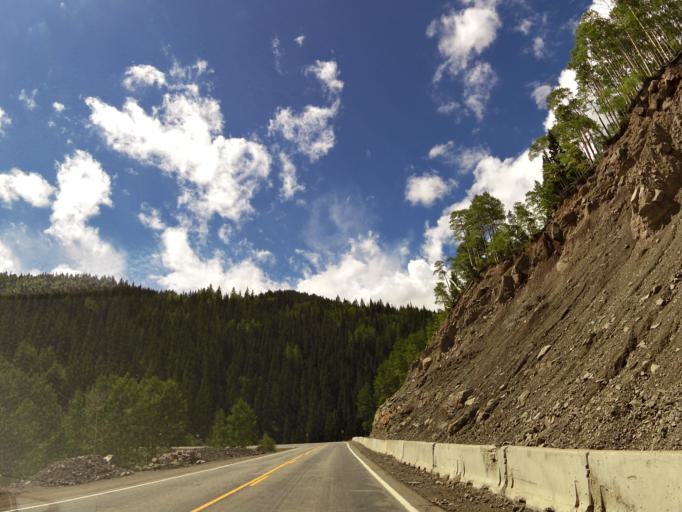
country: US
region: Colorado
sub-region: San Juan County
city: Silverton
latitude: 37.7193
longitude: -107.7548
